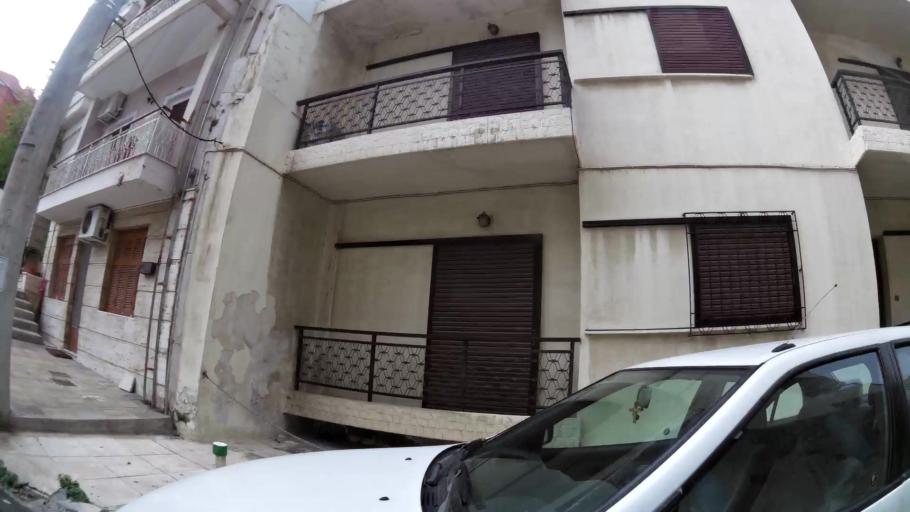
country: GR
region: Attica
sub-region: Nomarchia Athinas
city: Moskhaton
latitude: 37.9416
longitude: 23.6587
